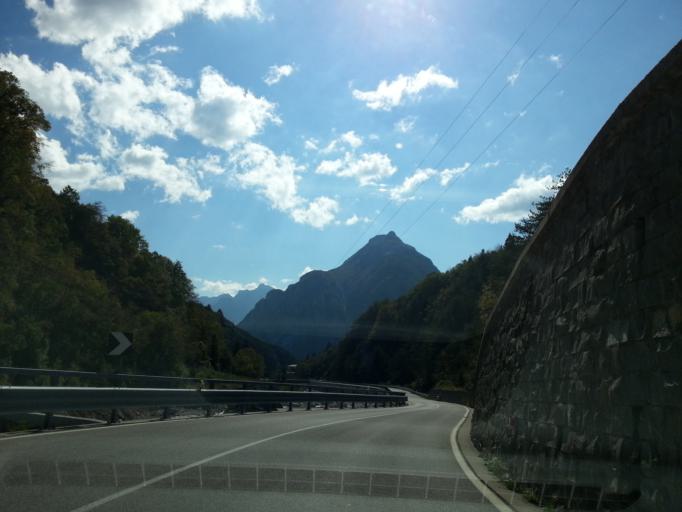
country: IT
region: Friuli Venezia Giulia
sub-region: Provincia di Udine
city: Moggio Udinese
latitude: 46.4682
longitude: 13.1908
